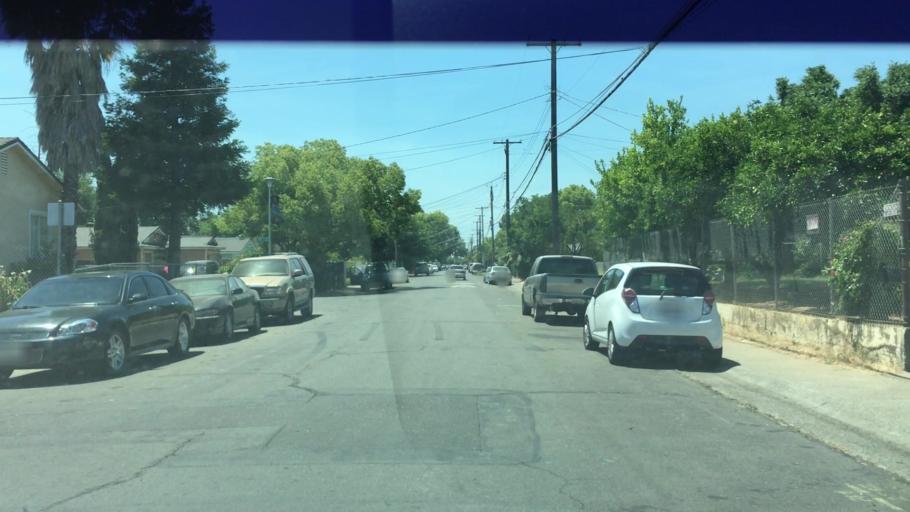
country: US
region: California
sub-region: Sacramento County
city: Florin
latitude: 38.5243
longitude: -121.4145
